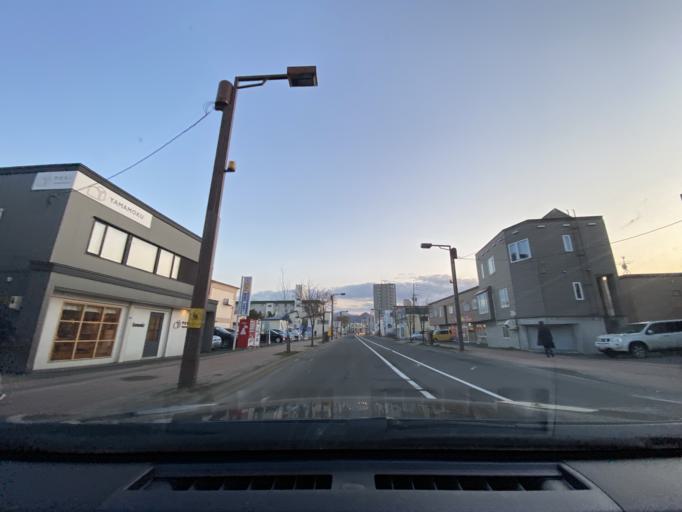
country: JP
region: Hokkaido
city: Sapporo
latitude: 43.0901
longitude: 141.3182
